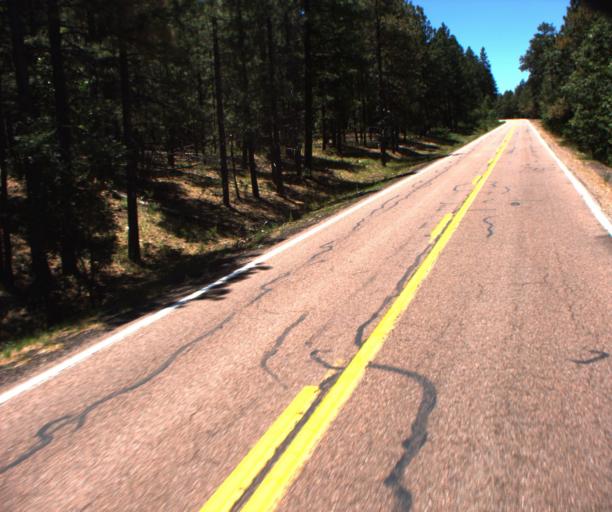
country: US
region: Arizona
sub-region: Gila County
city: Pine
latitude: 34.4867
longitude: -111.3770
